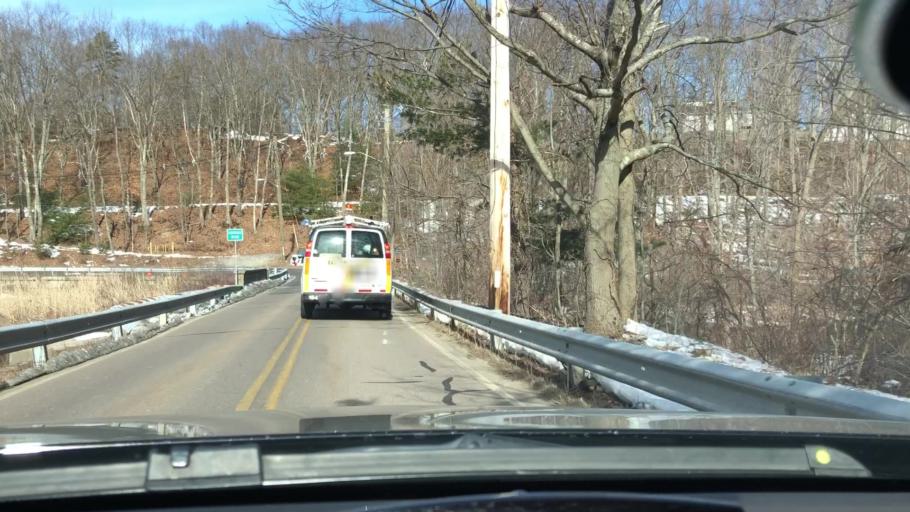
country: US
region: Massachusetts
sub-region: Norfolk County
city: Walpole
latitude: 42.1591
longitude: -71.2341
